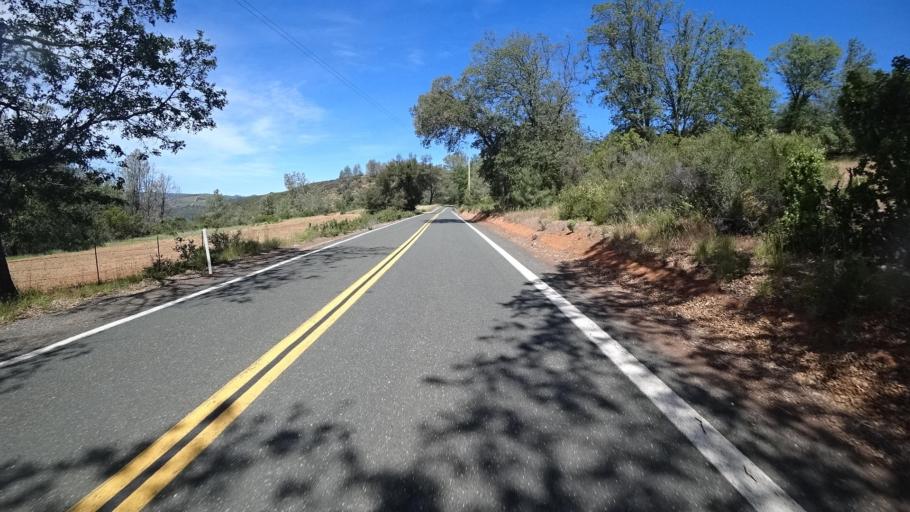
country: US
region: California
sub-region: Lake County
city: Clearlake
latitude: 38.9357
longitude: -122.6633
